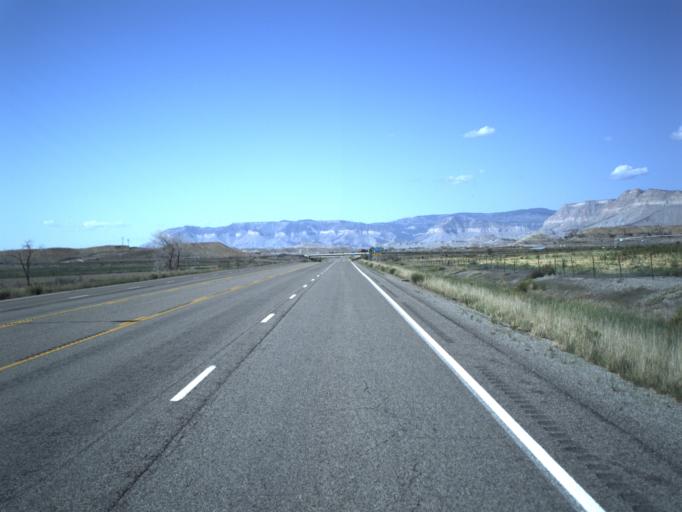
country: US
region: Utah
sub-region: Emery County
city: Castle Dale
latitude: 39.1813
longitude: -111.0392
